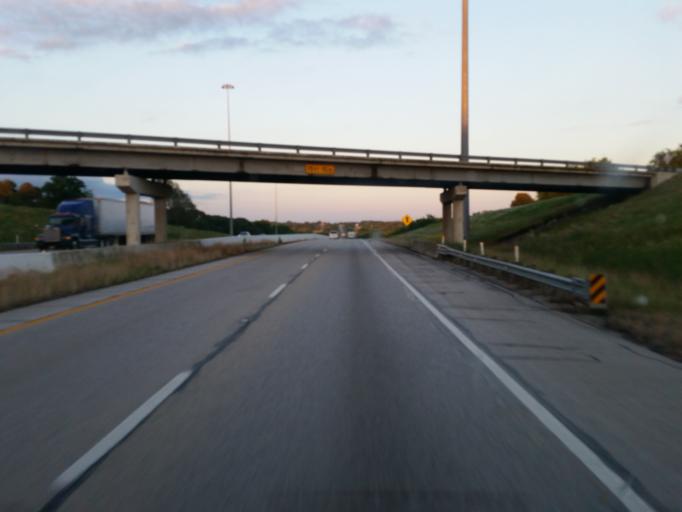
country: US
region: Texas
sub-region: Smith County
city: Hideaway
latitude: 32.4836
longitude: -95.5231
